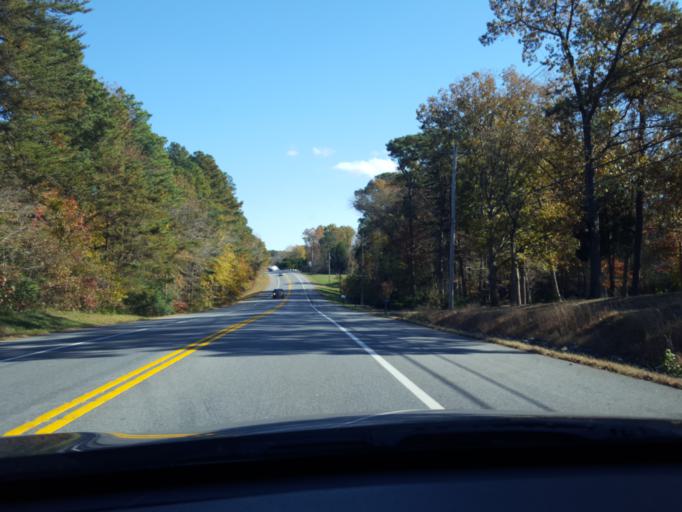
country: US
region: Maryland
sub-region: Saint Mary's County
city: California
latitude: 38.2398
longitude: -76.5558
